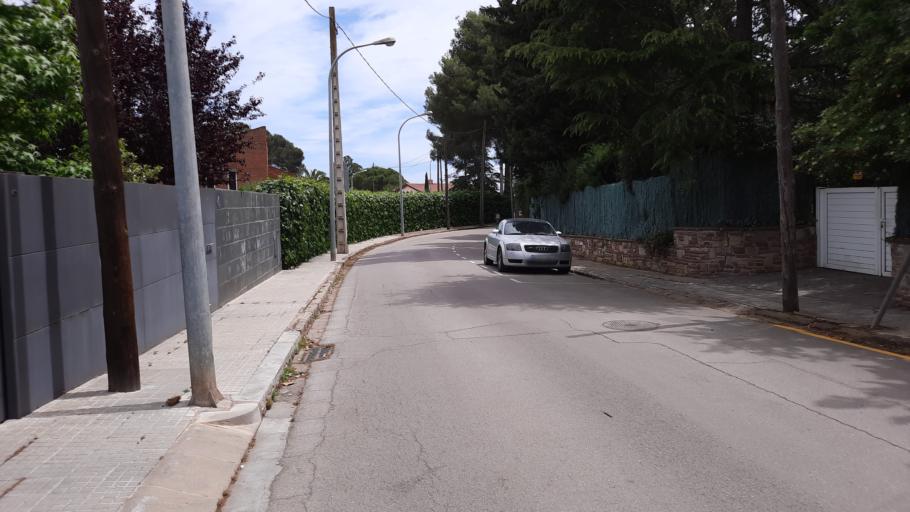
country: ES
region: Catalonia
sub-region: Provincia de Barcelona
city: Sant Quirze del Valles
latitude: 41.5054
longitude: 2.0857
